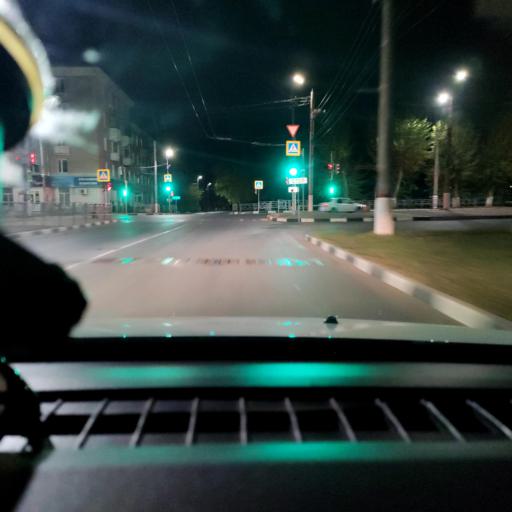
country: RU
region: Samara
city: Novokuybyshevsk
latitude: 53.1013
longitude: 49.9443
